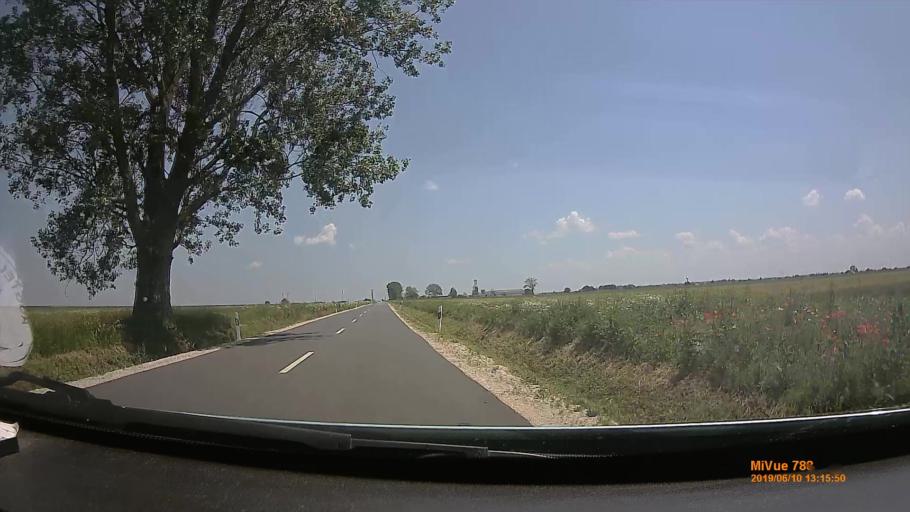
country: HU
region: Borsod-Abauj-Zemplen
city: Tiszaluc
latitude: 48.0483
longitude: 21.0451
